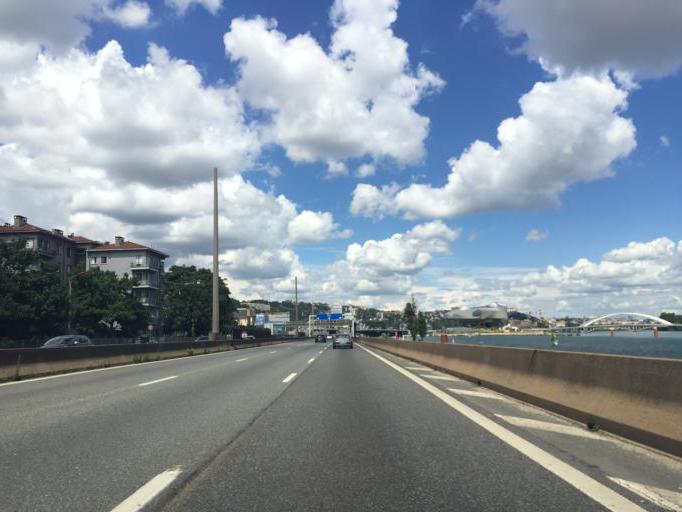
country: FR
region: Rhone-Alpes
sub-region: Departement du Rhone
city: La Mulatiere
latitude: 45.7244
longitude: 4.8175
